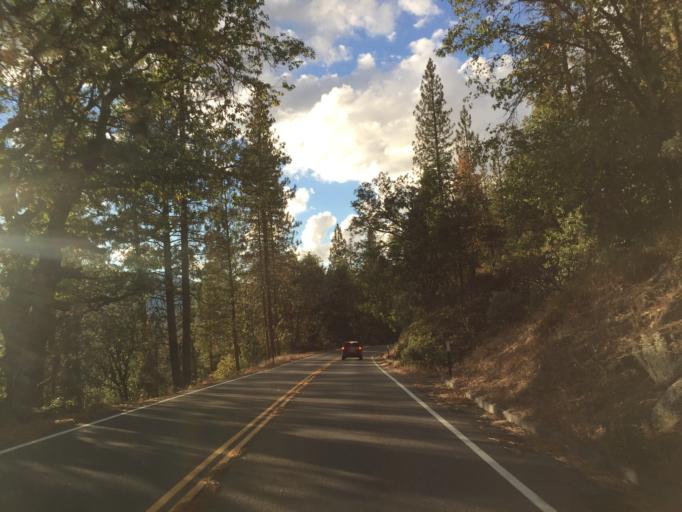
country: US
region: California
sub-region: Madera County
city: Ahwahnee
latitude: 37.5307
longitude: -119.6381
